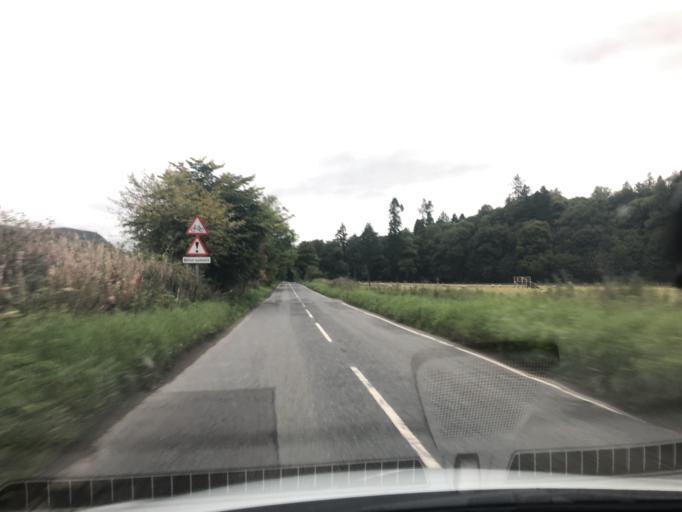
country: GB
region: Scotland
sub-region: Perth and Kinross
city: Pitlochry
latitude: 56.7465
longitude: -3.7855
